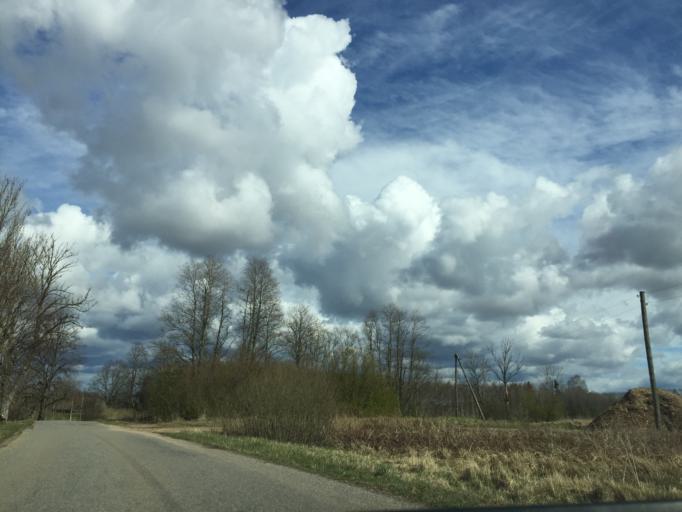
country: LV
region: Limbazu Rajons
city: Limbazi
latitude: 57.6128
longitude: 24.6740
